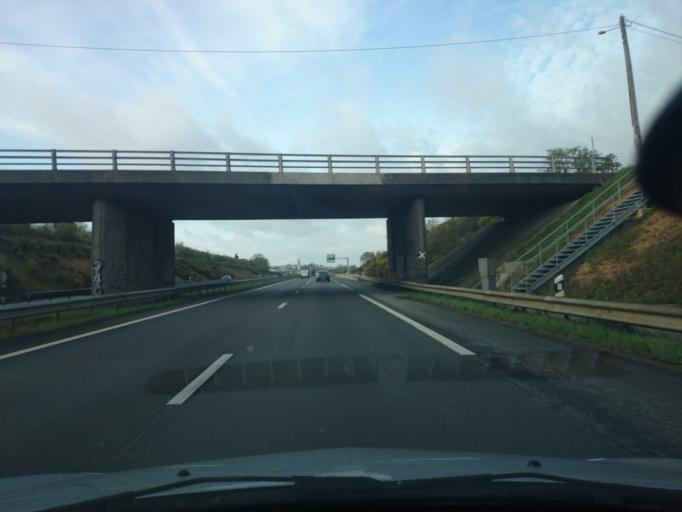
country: FR
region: Brittany
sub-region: Departement d'Ille-et-Vilaine
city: Montgermont
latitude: 48.1327
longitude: -1.7081
